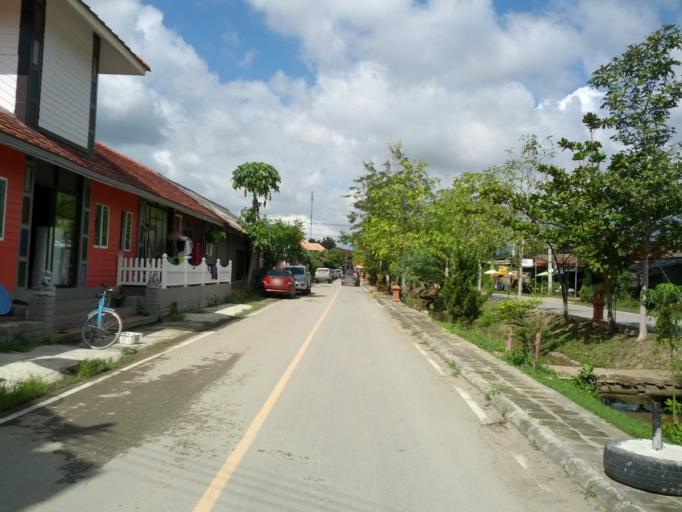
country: TH
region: Chiang Mai
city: Hang Dong
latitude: 18.6872
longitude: 98.9487
